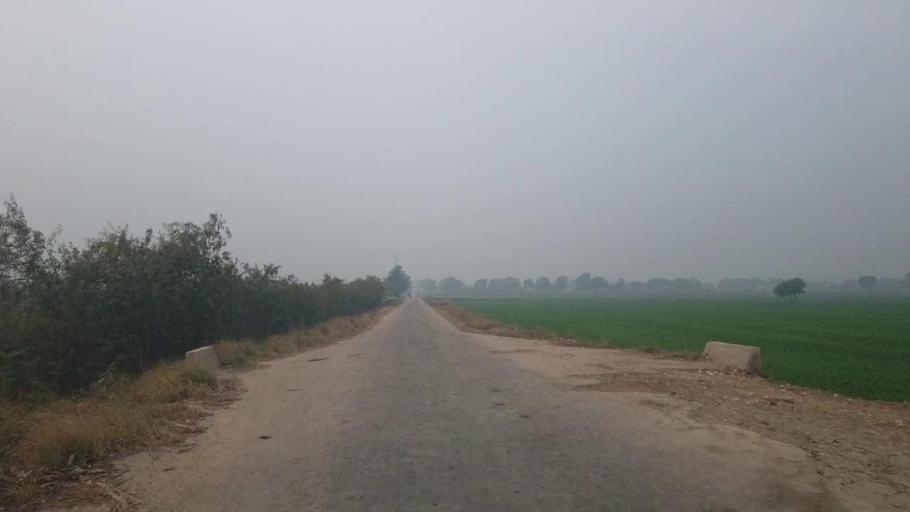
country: PK
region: Sindh
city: Tando Adam
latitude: 25.7097
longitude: 68.6666
